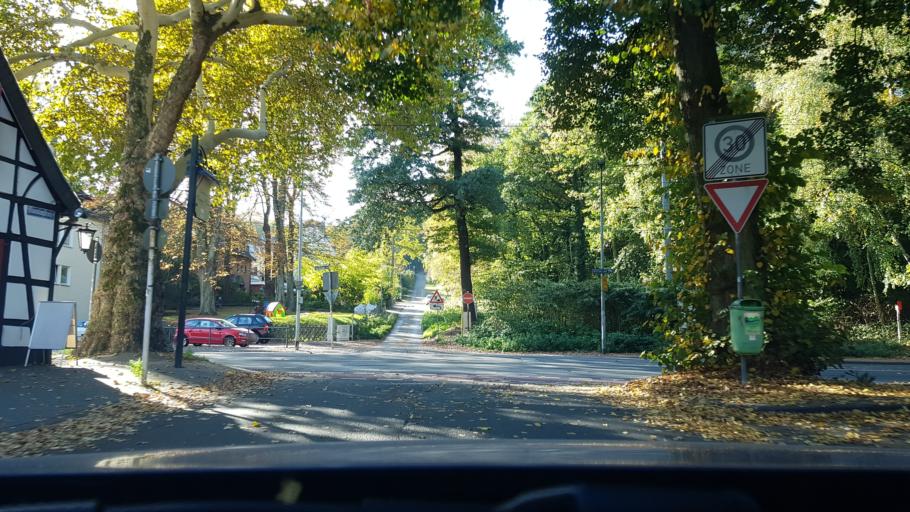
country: DE
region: North Rhine-Westphalia
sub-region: Regierungsbezirk Dusseldorf
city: Duisburg
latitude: 51.4332
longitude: 6.8182
